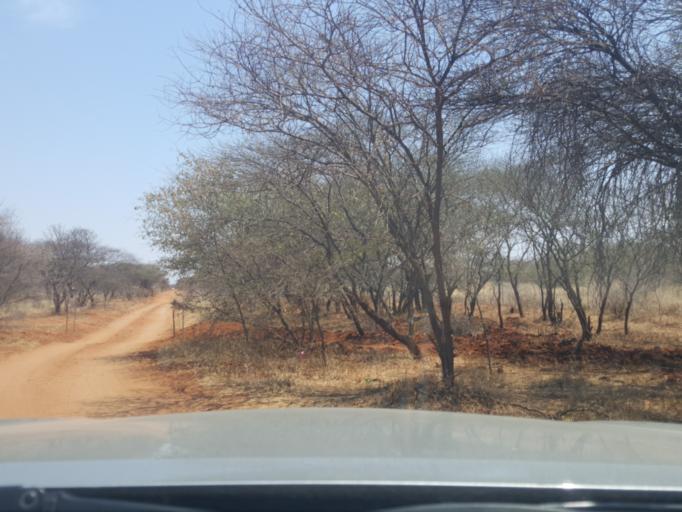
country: BW
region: South East
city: Ramotswa
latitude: -24.7736
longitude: 25.8452
